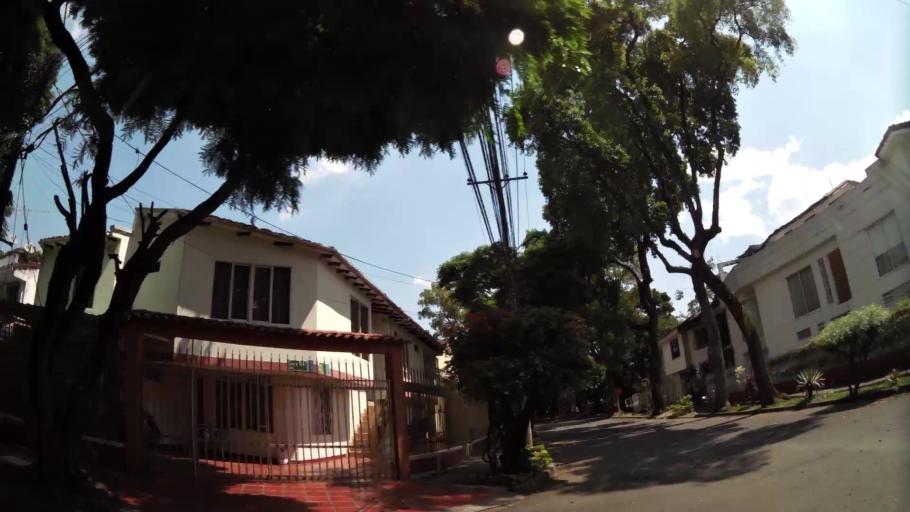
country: CO
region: Valle del Cauca
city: Cali
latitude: 3.4109
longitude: -76.5442
